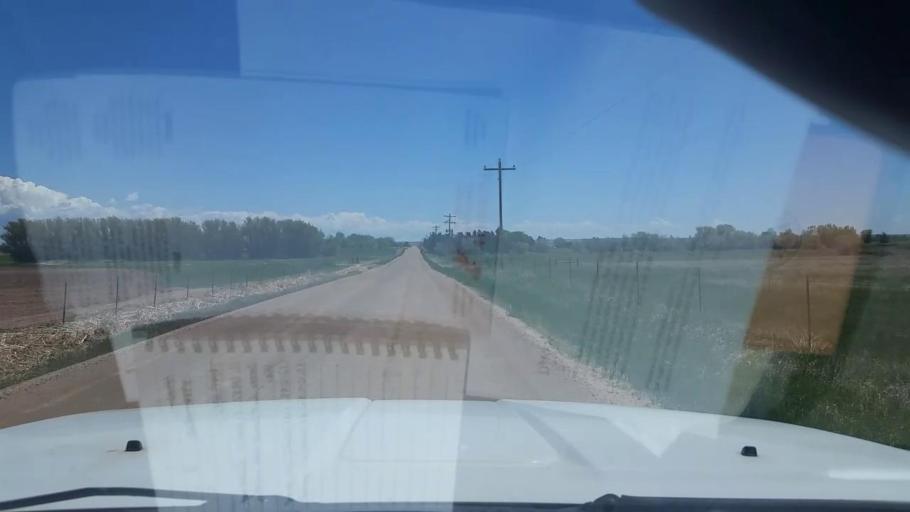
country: US
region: Colorado
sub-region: Larimer County
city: Wellington
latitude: 40.7981
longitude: -105.0703
